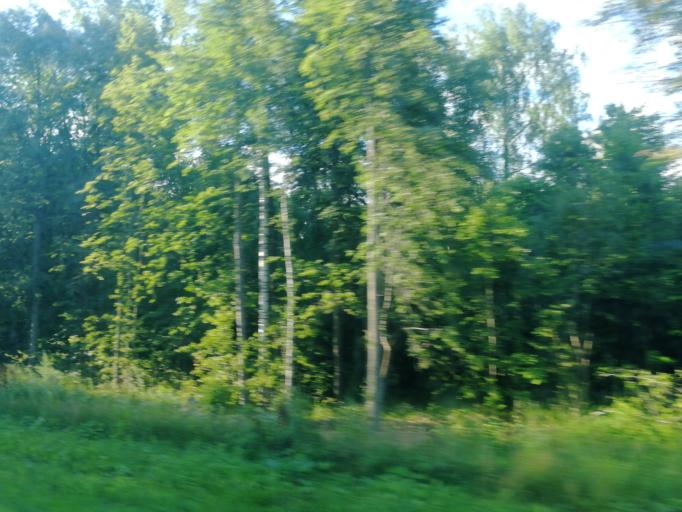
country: RU
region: Kaluga
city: Kaluga
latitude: 54.4440
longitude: 36.3205
